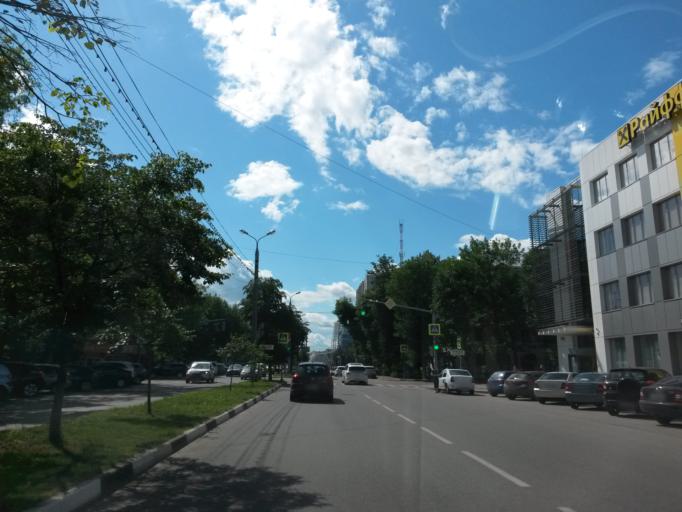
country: RU
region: Jaroslavl
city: Yaroslavl
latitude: 57.6332
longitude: 39.8709
